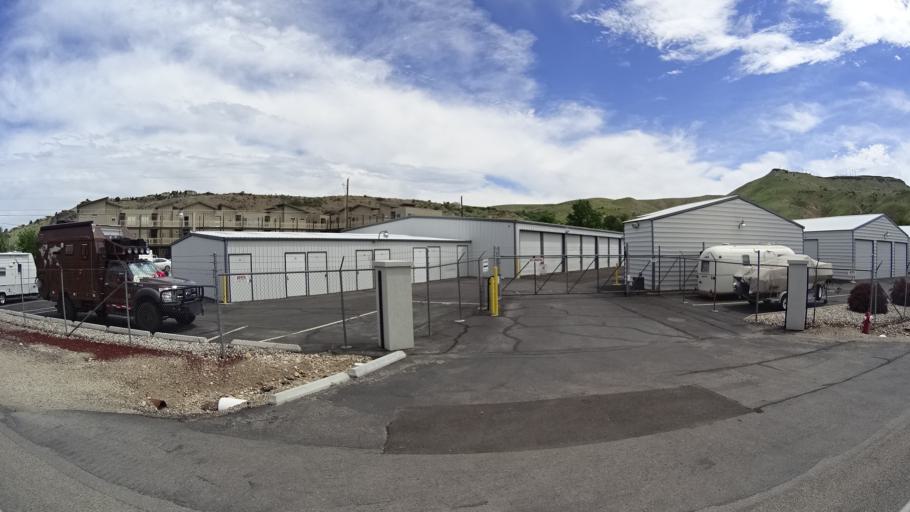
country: US
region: Idaho
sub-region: Ada County
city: Boise
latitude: 43.5996
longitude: -116.1665
